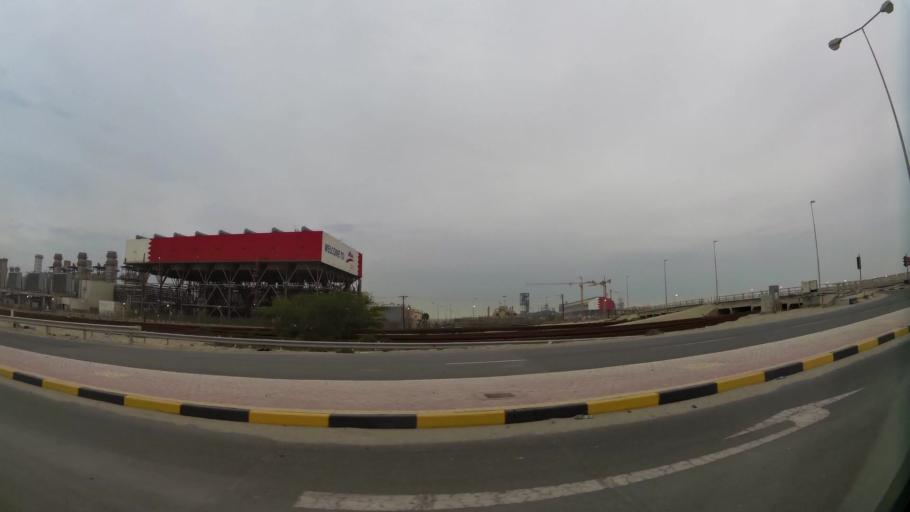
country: BH
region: Northern
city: Ar Rifa'
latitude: 26.0951
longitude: 50.5960
